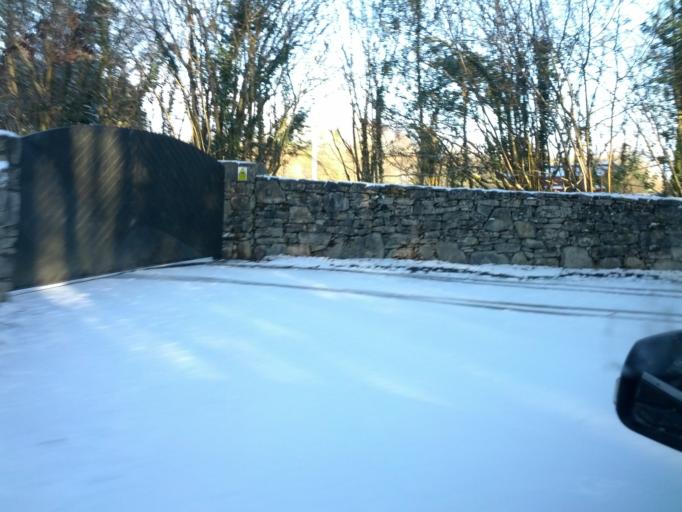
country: IE
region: Connaught
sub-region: County Galway
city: Gort
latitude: 53.1826
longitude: -8.8067
